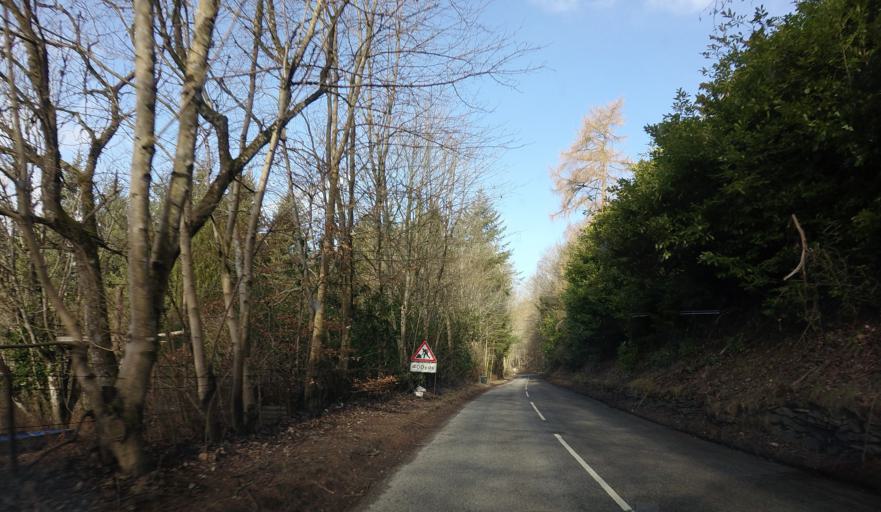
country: GB
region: Scotland
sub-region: Perth and Kinross
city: Bankfoot
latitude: 56.5906
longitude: -3.6205
